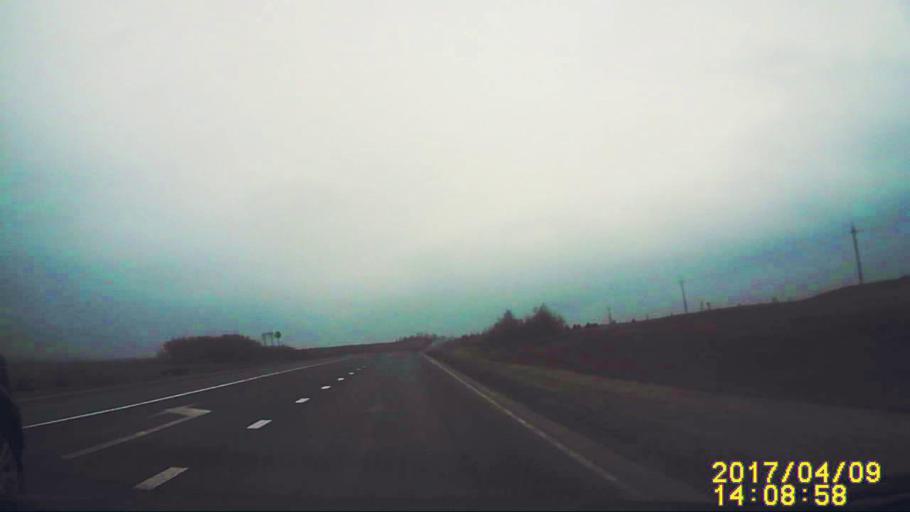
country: RU
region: Ulyanovsk
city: Silikatnyy
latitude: 54.0241
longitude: 48.2142
